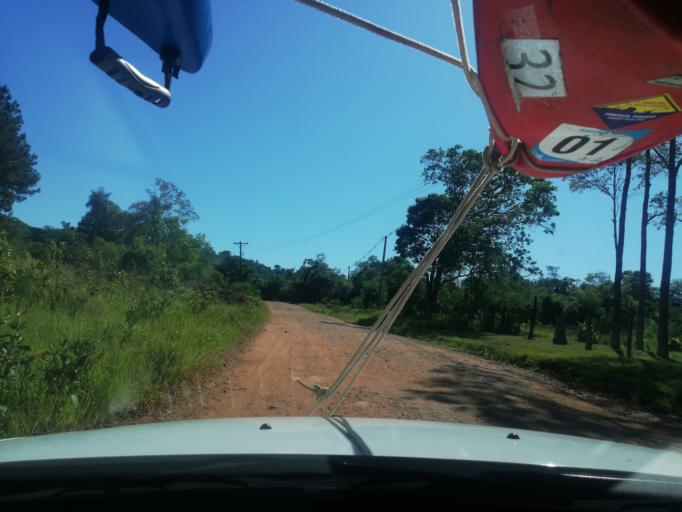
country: AR
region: Misiones
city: Santa Ana
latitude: -27.3366
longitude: -55.5835
